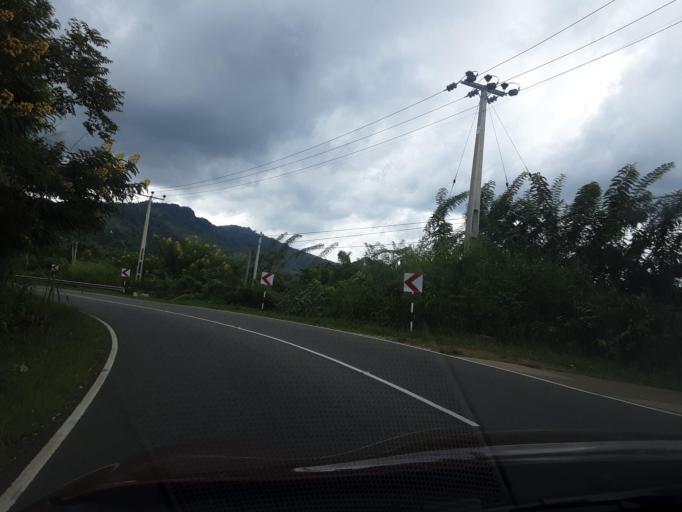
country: LK
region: Uva
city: Monaragala
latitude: 6.9097
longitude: 81.2137
